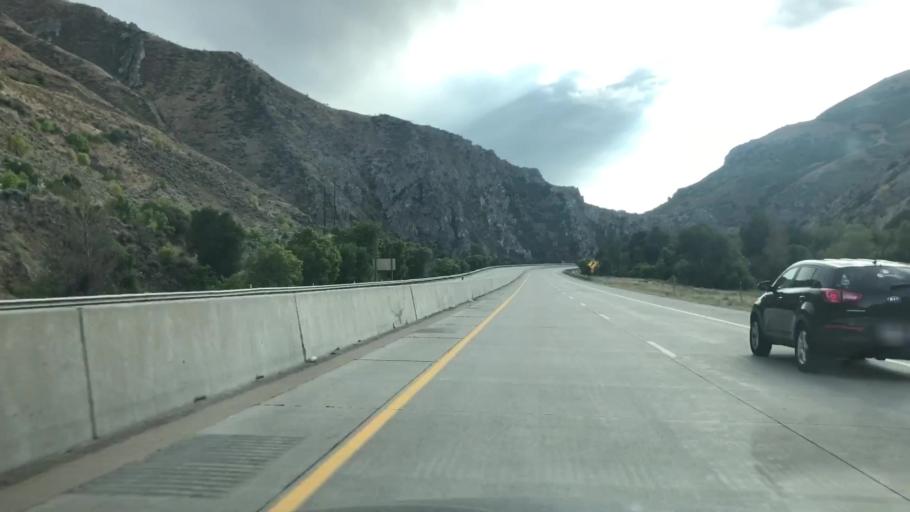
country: US
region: Utah
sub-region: Morgan County
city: Morgan
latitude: 41.0598
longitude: -111.5784
